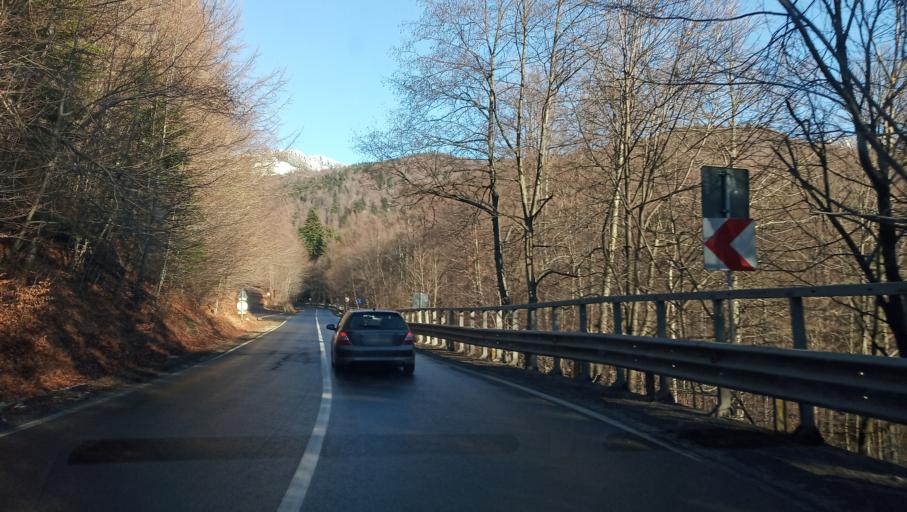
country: RO
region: Brasov
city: Crivina
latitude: 45.4688
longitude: 25.9310
